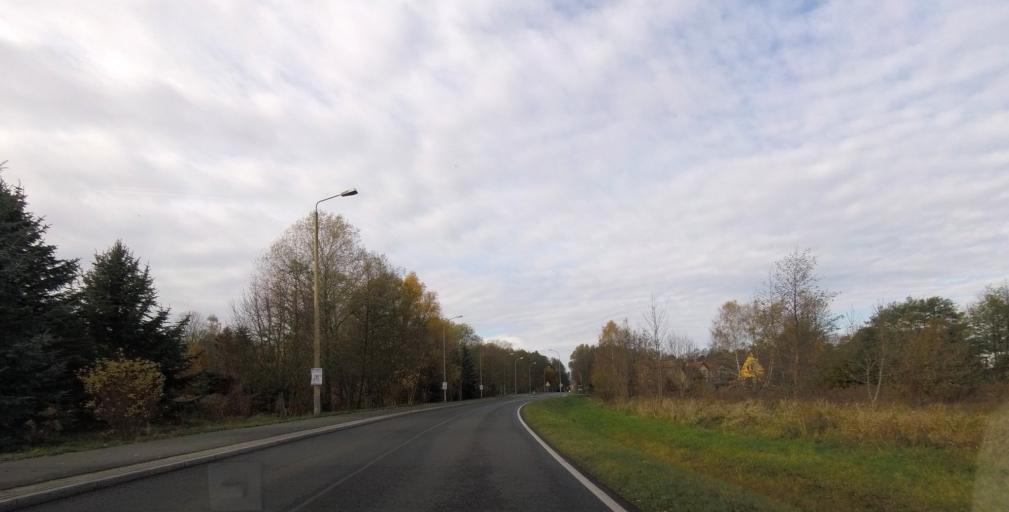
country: DE
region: Brandenburg
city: Treuenbrietzen
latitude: 52.0910
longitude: 12.8699
